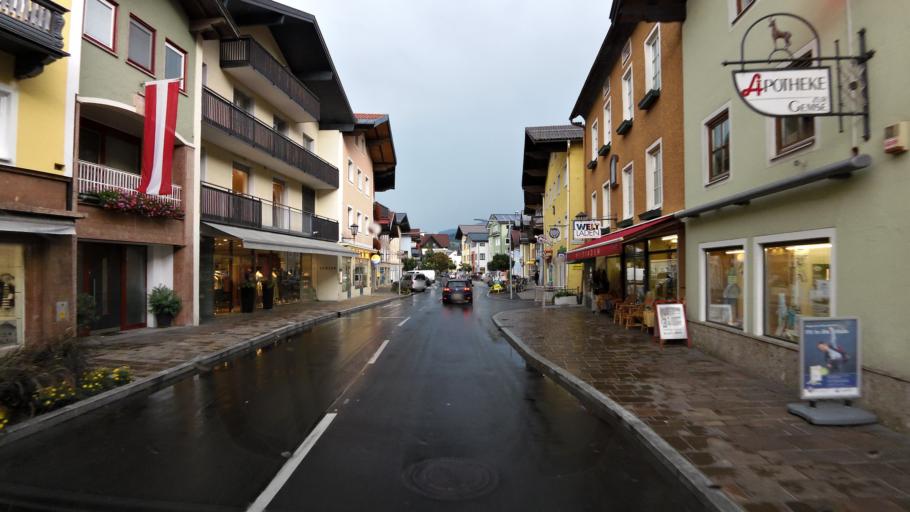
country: AT
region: Salzburg
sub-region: Politischer Bezirk Hallein
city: Golling an der Salzach
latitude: 47.5988
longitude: 13.1681
